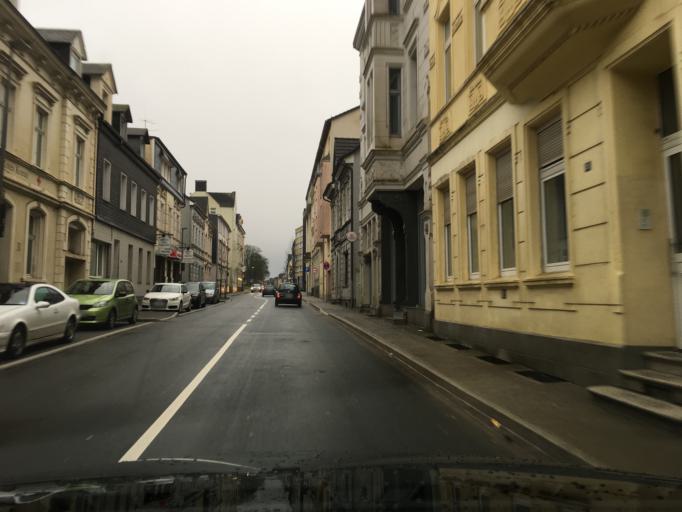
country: DE
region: North Rhine-Westphalia
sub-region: Regierungsbezirk Dusseldorf
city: Velbert
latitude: 51.3412
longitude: 7.0477
